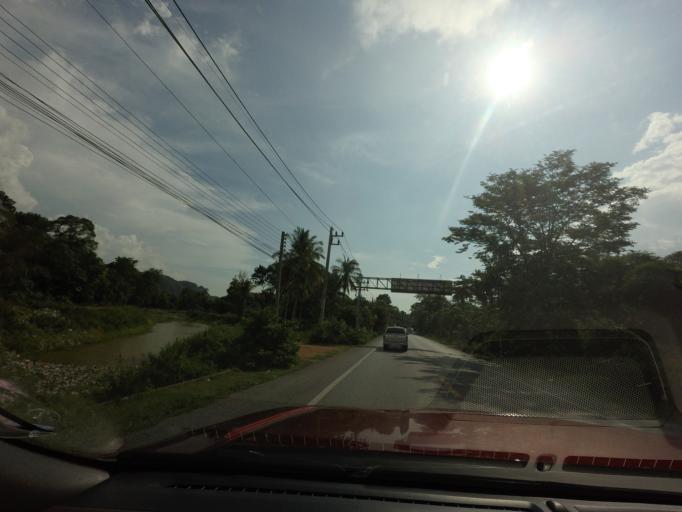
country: TH
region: Yala
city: Yala
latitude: 6.5479
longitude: 101.2431
